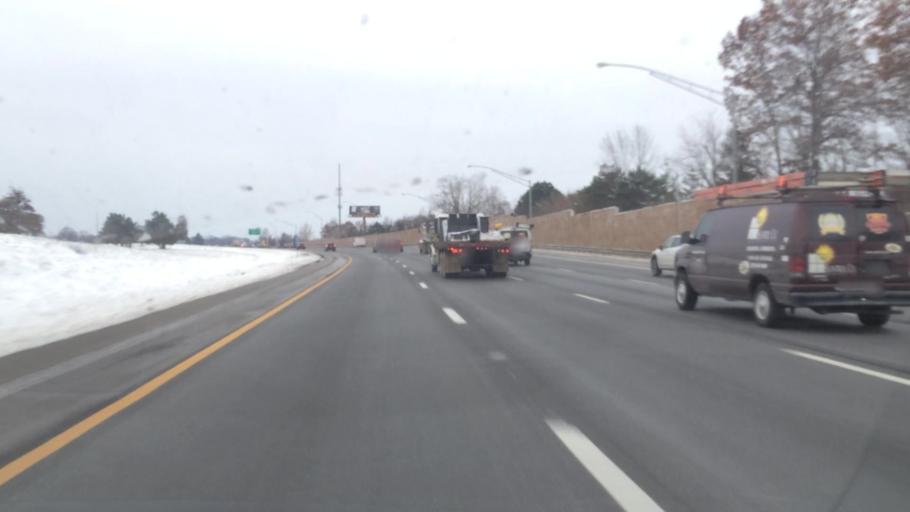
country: US
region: Ohio
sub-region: Cuyahoga County
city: Garfield Heights
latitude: 41.4206
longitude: -81.5891
